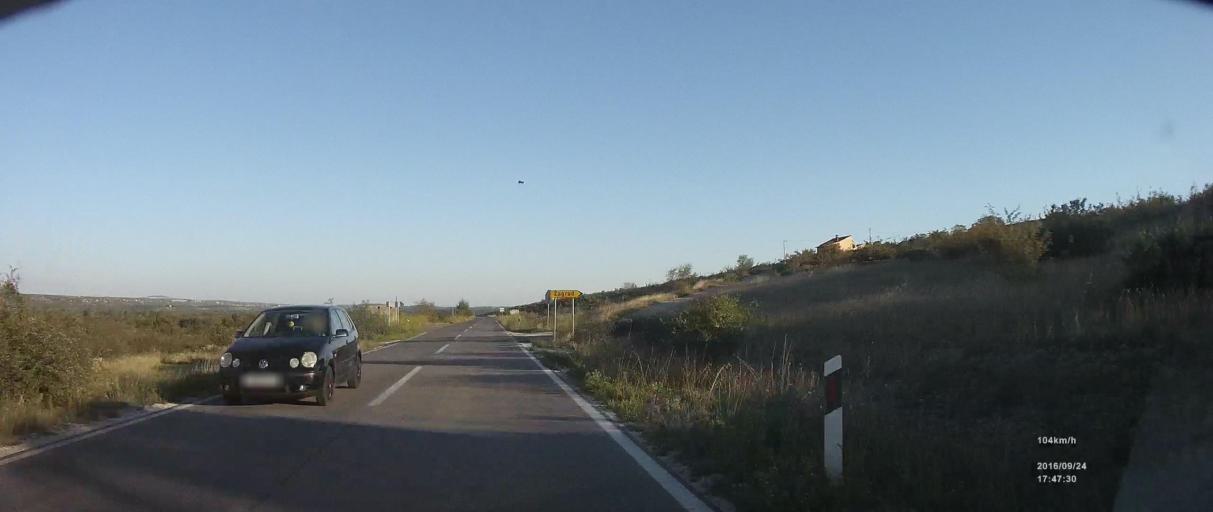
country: HR
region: Zadarska
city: Polaca
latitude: 44.0746
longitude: 15.5238
